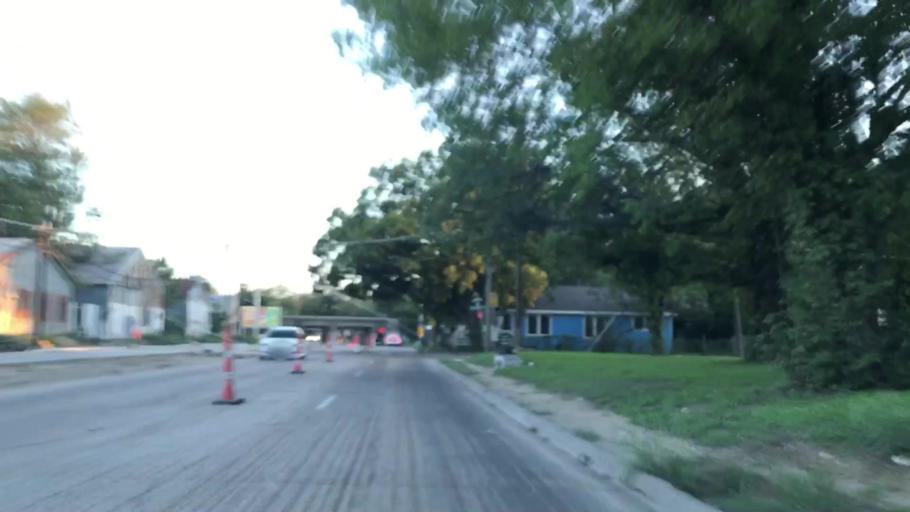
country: US
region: Texas
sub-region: Dallas County
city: Dallas
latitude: 32.7762
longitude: -96.8359
